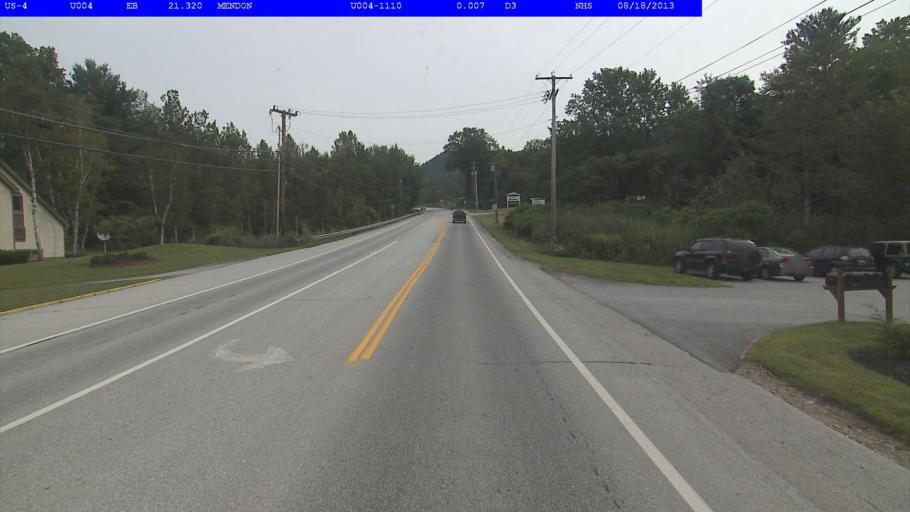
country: US
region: Vermont
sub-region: Rutland County
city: Rutland
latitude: 43.6350
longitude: -72.9373
